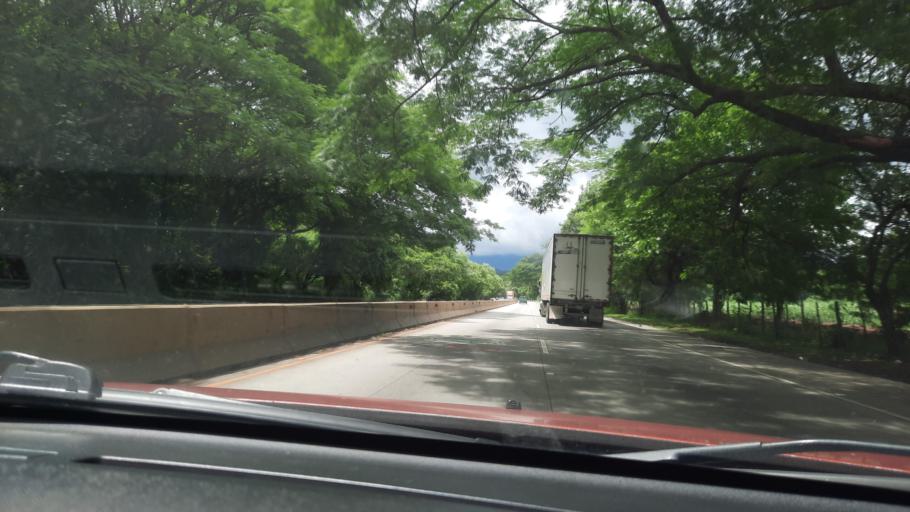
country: SV
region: Sonsonate
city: Sonzacate
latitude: 13.7260
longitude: -89.7035
